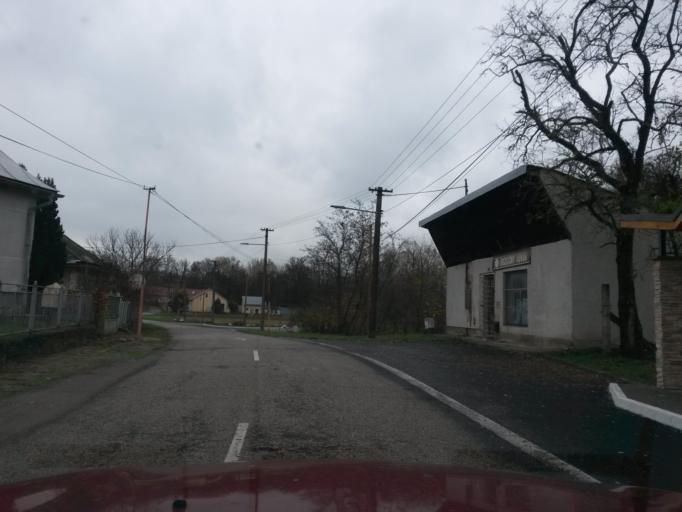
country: SK
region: Kosicky
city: Cierna nad Tisou
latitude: 48.5584
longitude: 21.9575
